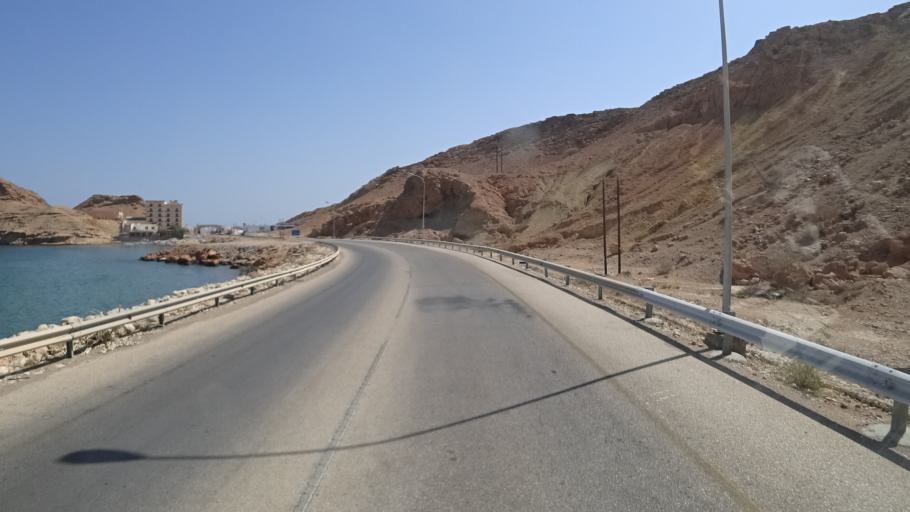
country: OM
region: Ash Sharqiyah
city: Sur
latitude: 22.5572
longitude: 59.5401
